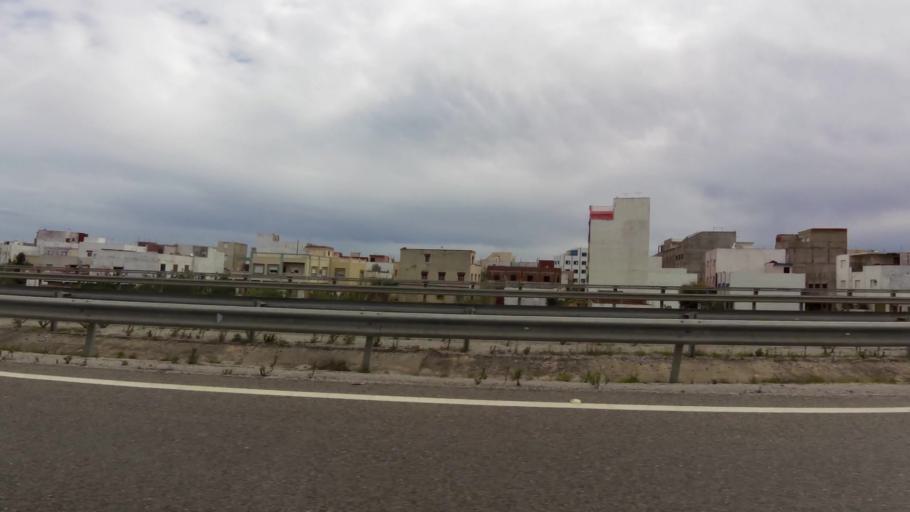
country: MA
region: Tanger-Tetouan
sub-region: Tetouan
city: Martil
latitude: 35.6997
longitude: -5.3522
